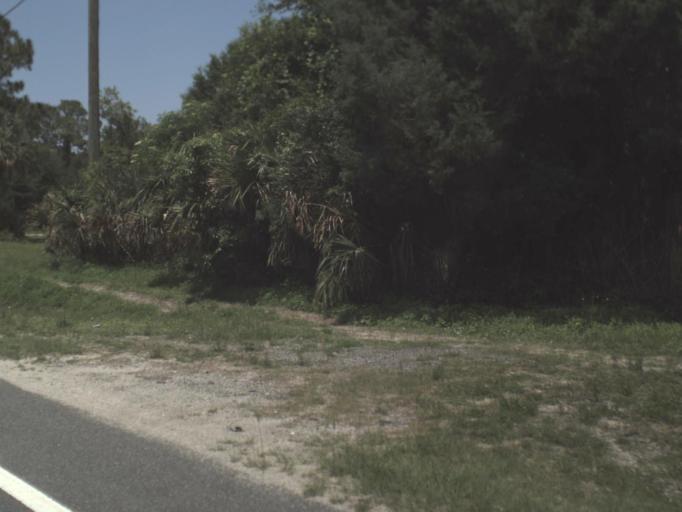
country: US
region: Florida
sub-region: Nassau County
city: Yulee
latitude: 30.5110
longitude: -81.6227
